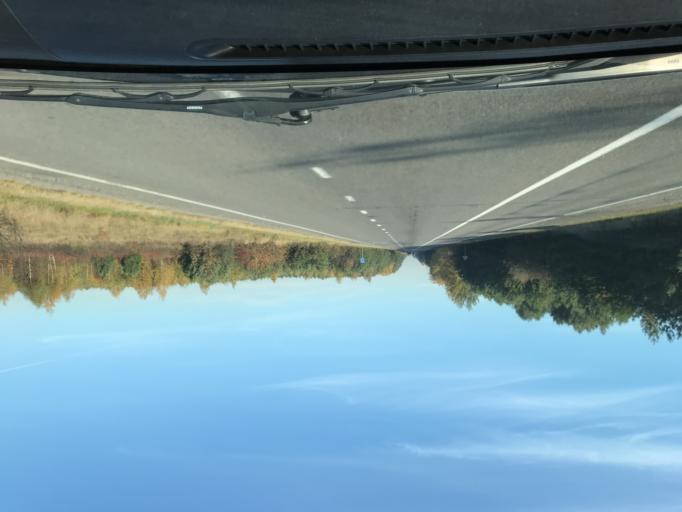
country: BY
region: Brest
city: Davyd-Haradok
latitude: 52.2450
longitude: 27.1376
